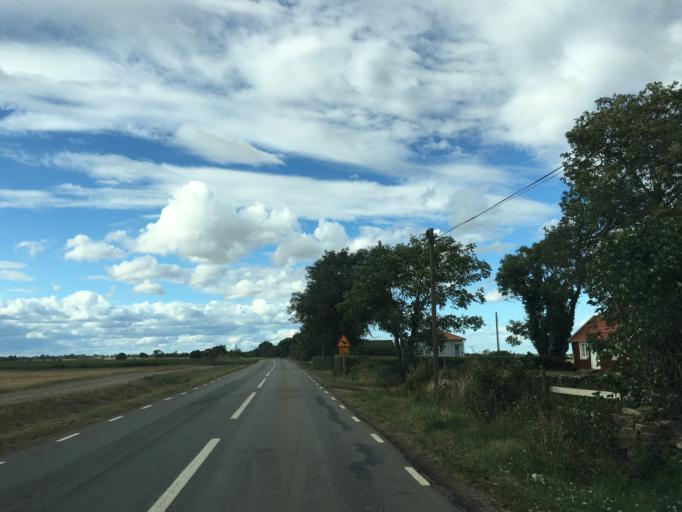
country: SE
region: Kalmar
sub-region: Morbylanga Kommun
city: Moerbylanga
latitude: 56.4213
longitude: 16.4356
